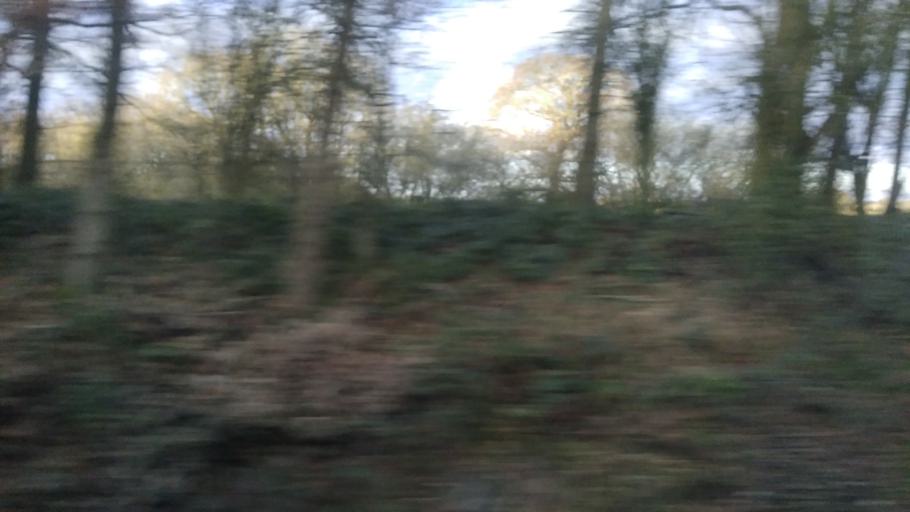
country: GB
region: England
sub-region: Kent
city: Headcorn
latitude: 51.1617
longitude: 0.6803
